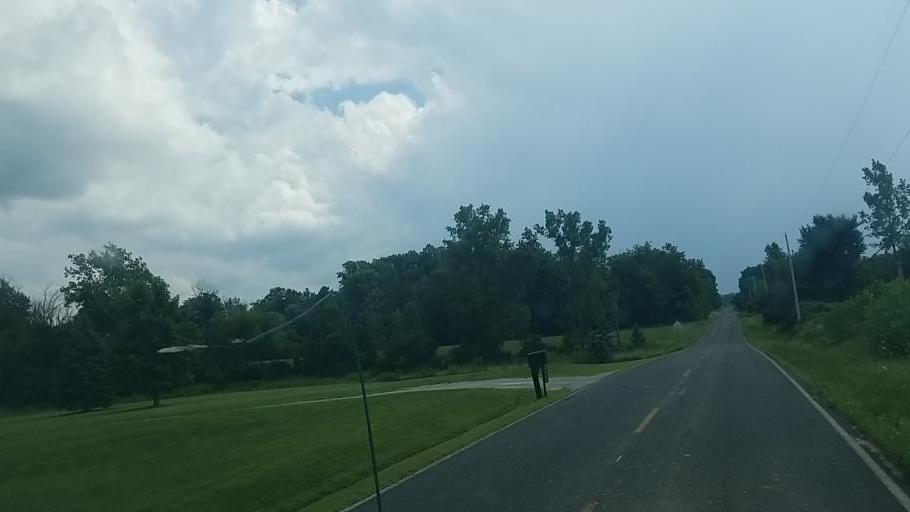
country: US
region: Ohio
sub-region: Medina County
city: Medina
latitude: 41.1412
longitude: -81.9545
